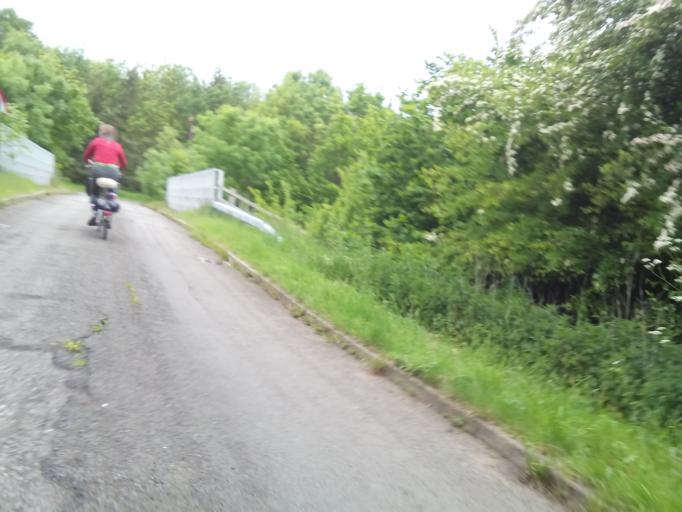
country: GB
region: England
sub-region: District of Rutland
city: South Luffenham
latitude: 52.5389
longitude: -0.5901
